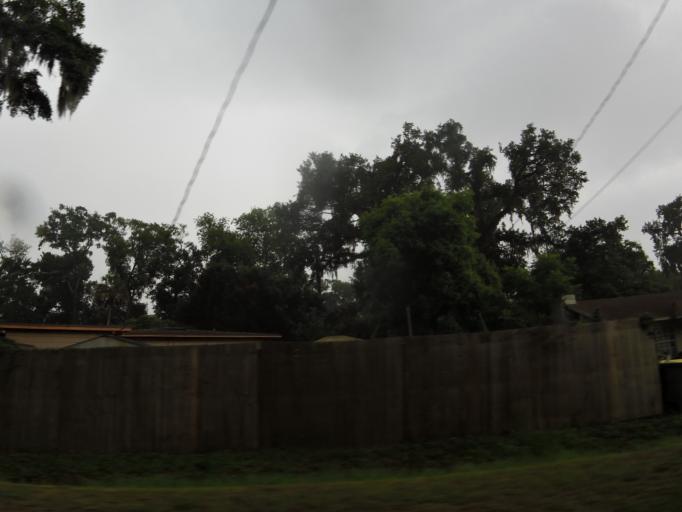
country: US
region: Florida
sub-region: Duval County
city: Jacksonville
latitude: 30.3430
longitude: -81.6071
